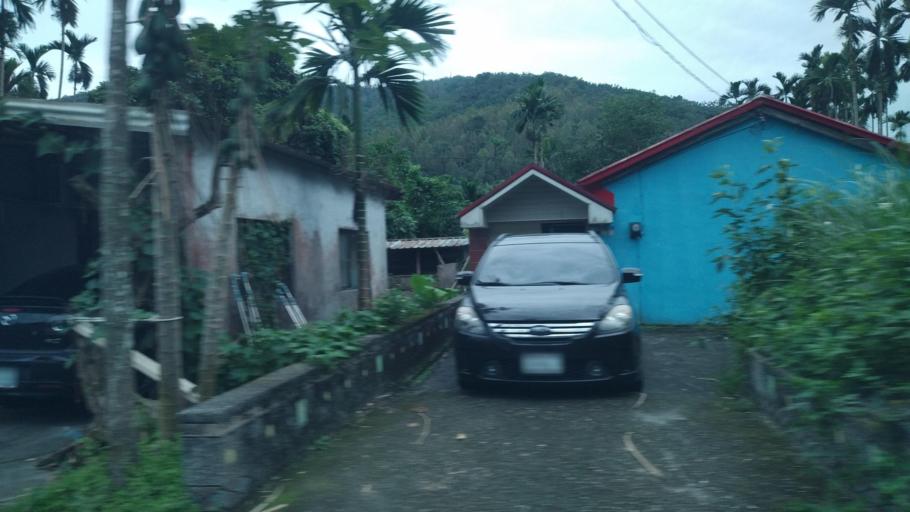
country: TW
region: Taiwan
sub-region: Hualien
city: Hualian
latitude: 23.9232
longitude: 121.5050
